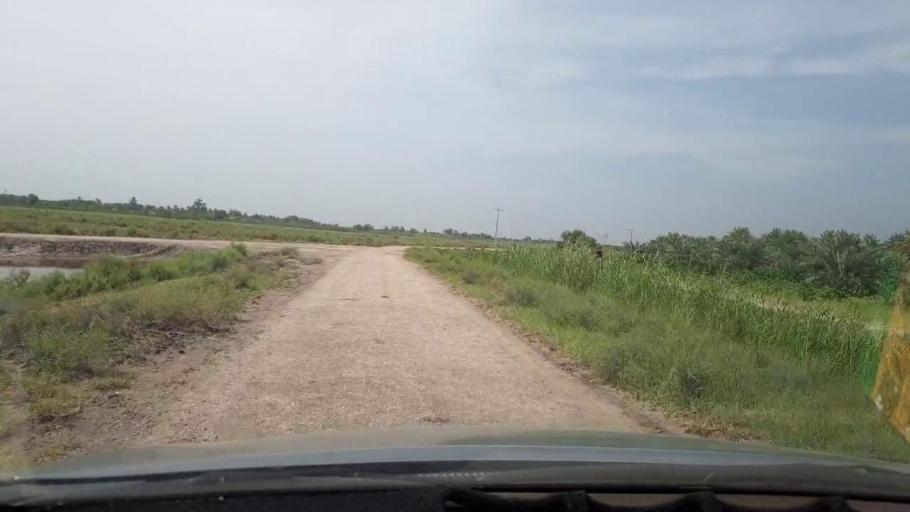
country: PK
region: Sindh
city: Khairpur
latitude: 27.4762
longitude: 68.7441
